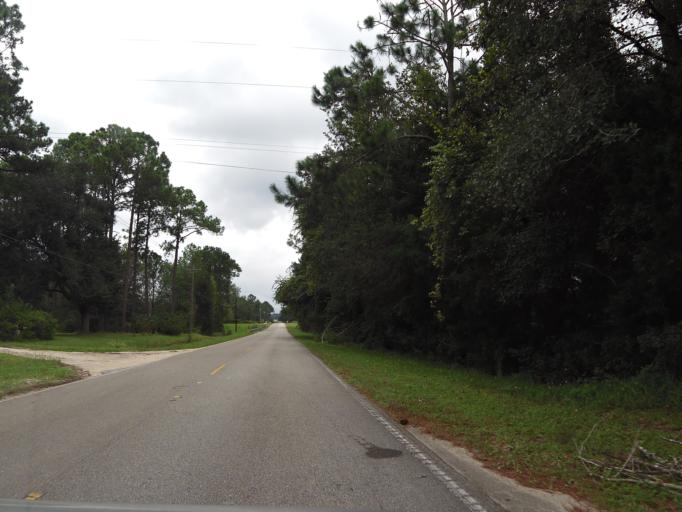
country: US
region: Florida
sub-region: Clay County
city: Middleburg
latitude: 30.1130
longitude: -81.9491
